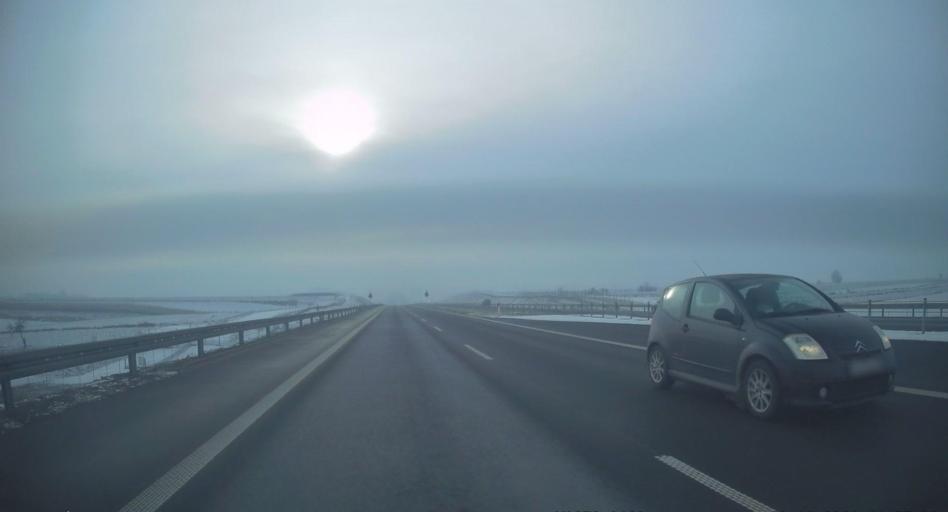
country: PL
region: Lesser Poland Voivodeship
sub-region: Powiat miechowski
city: Miechow
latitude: 50.2905
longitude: 20.0250
